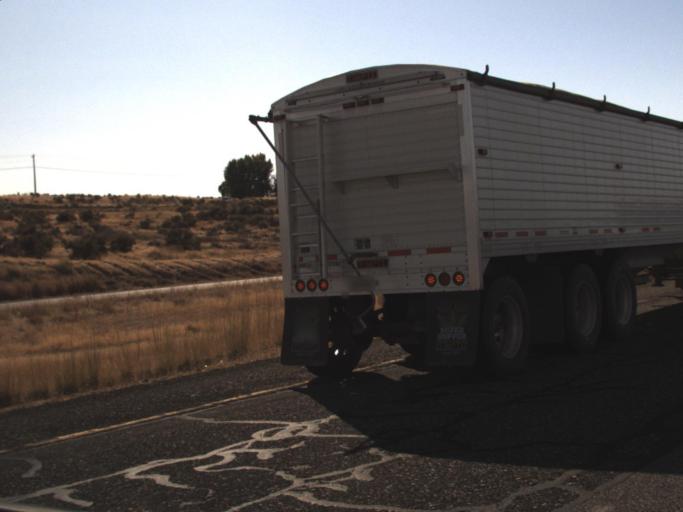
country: US
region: Washington
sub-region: Franklin County
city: Basin City
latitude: 46.4495
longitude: -119.0175
